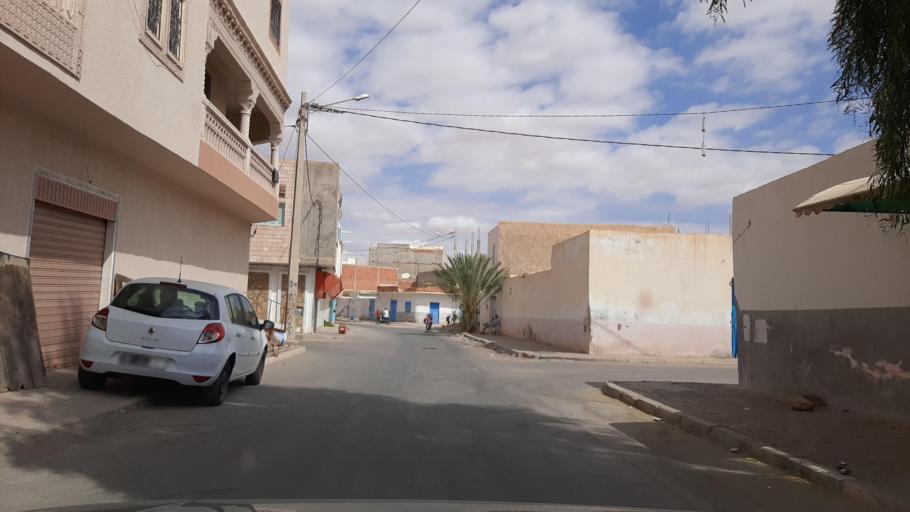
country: TN
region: Tataouine
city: Tataouine
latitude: 32.9274
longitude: 10.4554
